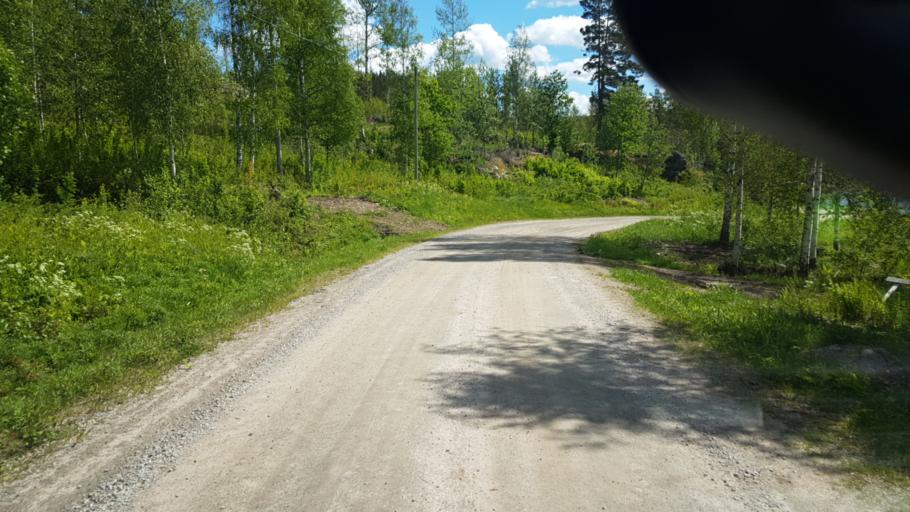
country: SE
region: Vaermland
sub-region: Arvika Kommun
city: Arvika
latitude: 59.7135
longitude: 12.8485
